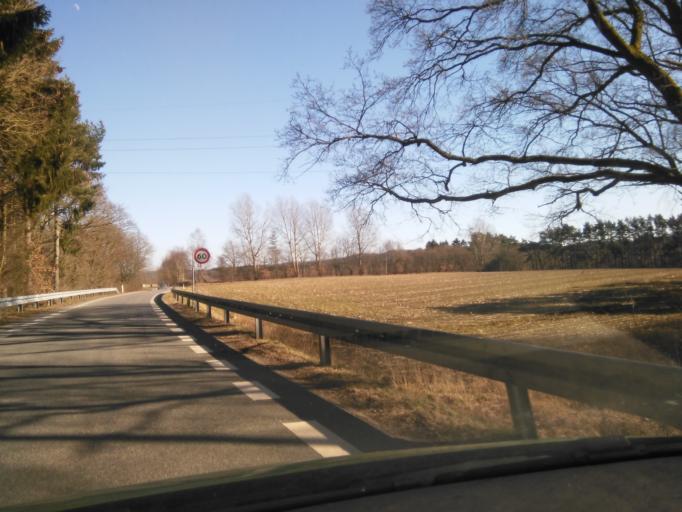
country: DK
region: Central Jutland
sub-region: Skanderborg Kommune
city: Ry
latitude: 56.1092
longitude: 9.7981
